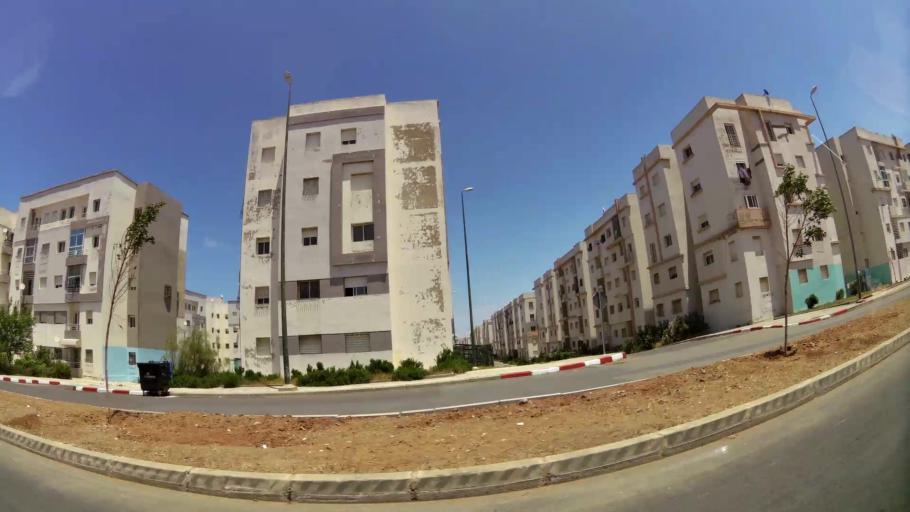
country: MA
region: Gharb-Chrarda-Beni Hssen
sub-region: Kenitra Province
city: Kenitra
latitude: 34.2508
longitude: -6.6434
